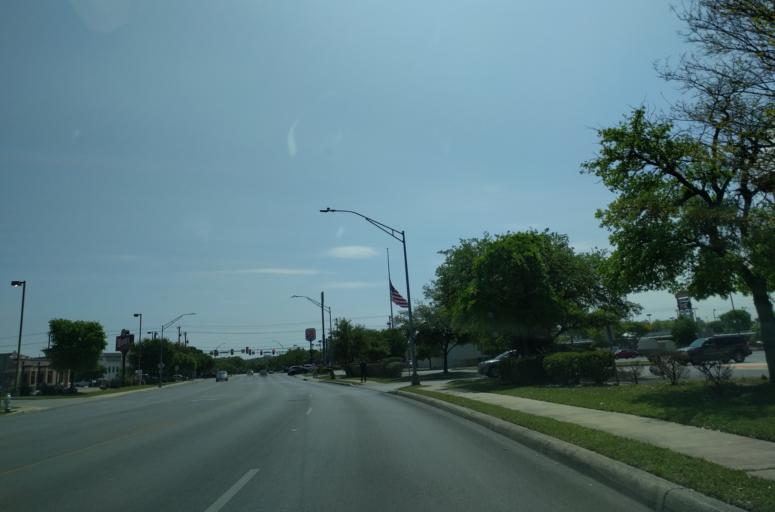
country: US
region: Texas
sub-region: Bexar County
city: Shavano Park
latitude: 29.5661
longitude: -98.5868
